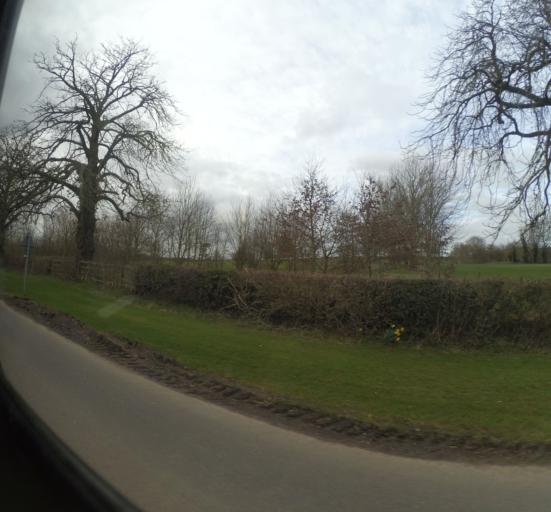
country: GB
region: England
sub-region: Warwickshire
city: Long Lawford
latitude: 52.4121
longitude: -1.3229
